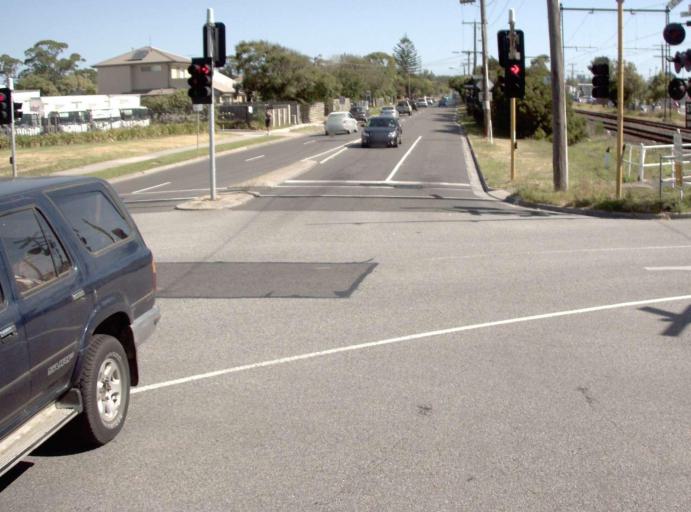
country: AU
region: Victoria
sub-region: Frankston
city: Frankston East
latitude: -38.1301
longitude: 145.1319
